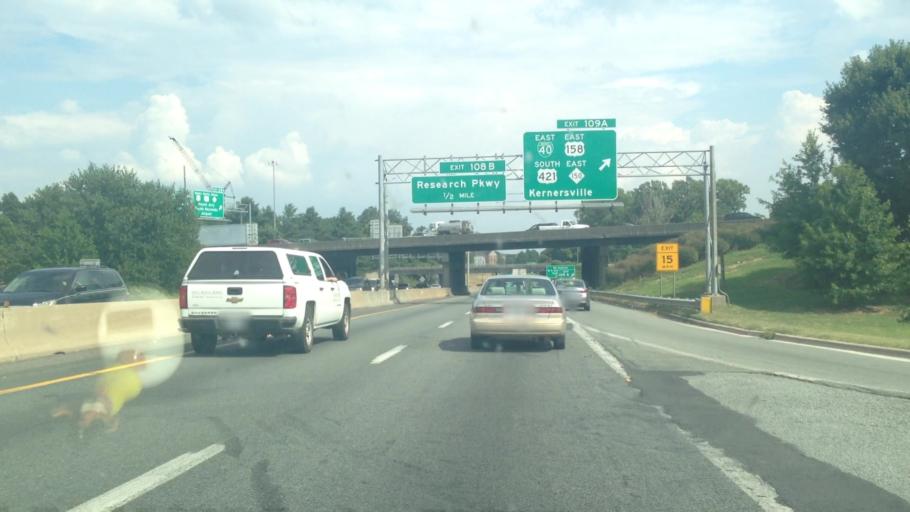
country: US
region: North Carolina
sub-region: Forsyth County
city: Winston-Salem
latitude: 36.0948
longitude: -80.2335
